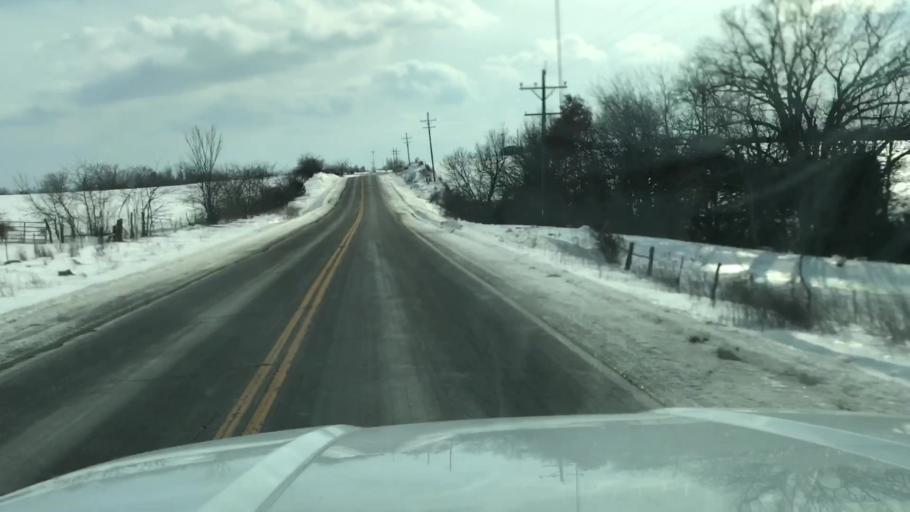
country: US
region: Missouri
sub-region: Gentry County
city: Stanberry
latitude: 40.3730
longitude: -94.6473
